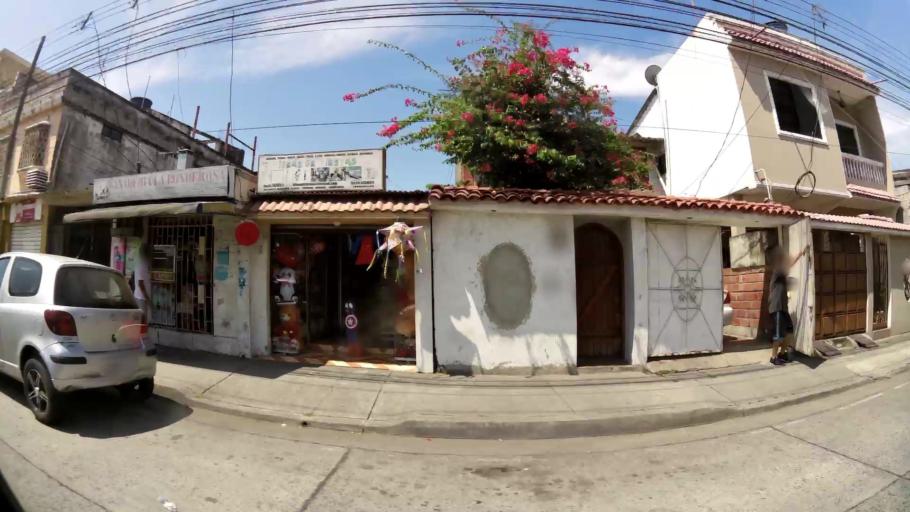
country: EC
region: Guayas
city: Eloy Alfaro
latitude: -2.1269
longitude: -79.9053
